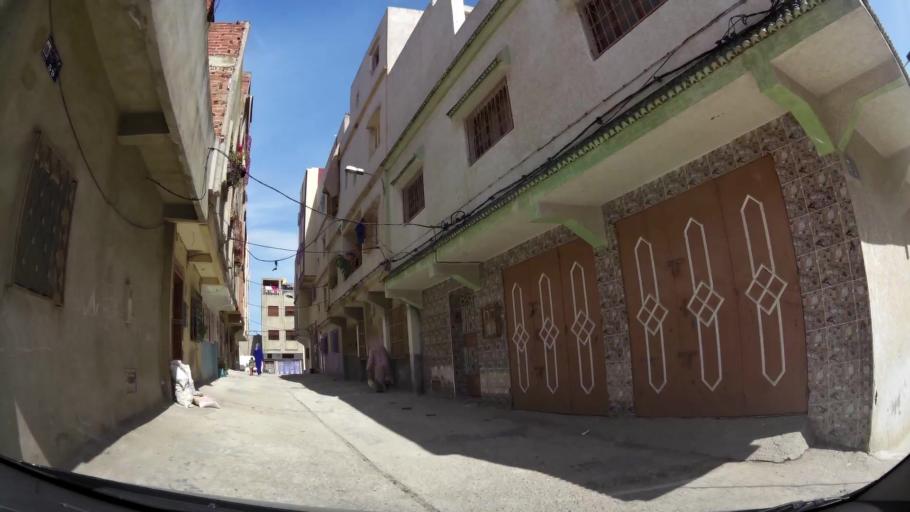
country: MA
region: Tanger-Tetouan
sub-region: Tanger-Assilah
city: Tangier
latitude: 35.7403
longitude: -5.8041
